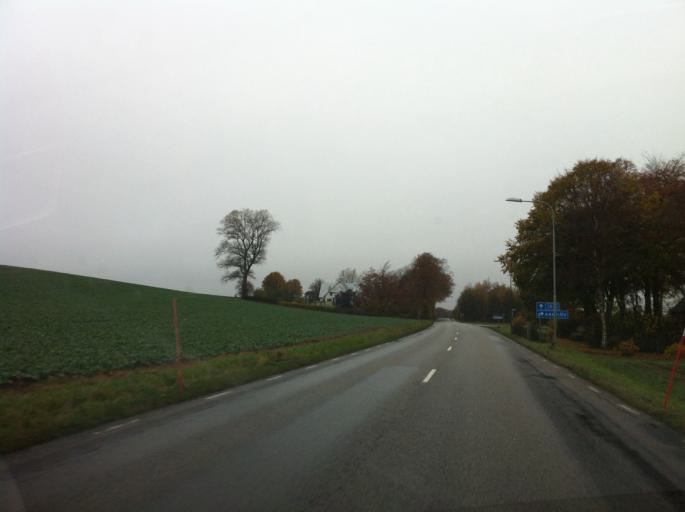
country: SE
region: Skane
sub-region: Kavlinge Kommun
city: Loddekopinge
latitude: 55.8162
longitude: 13.0449
